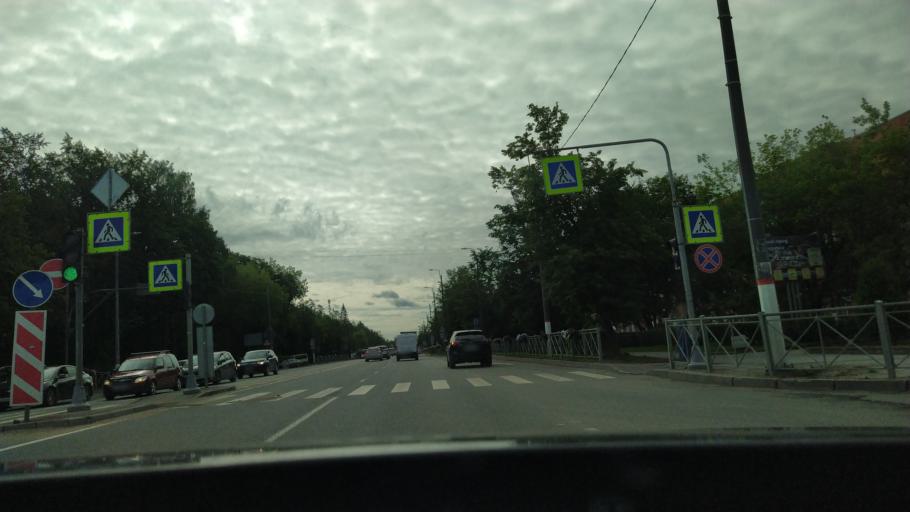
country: RU
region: Leningrad
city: Tosno
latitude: 59.5450
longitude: 30.8695
